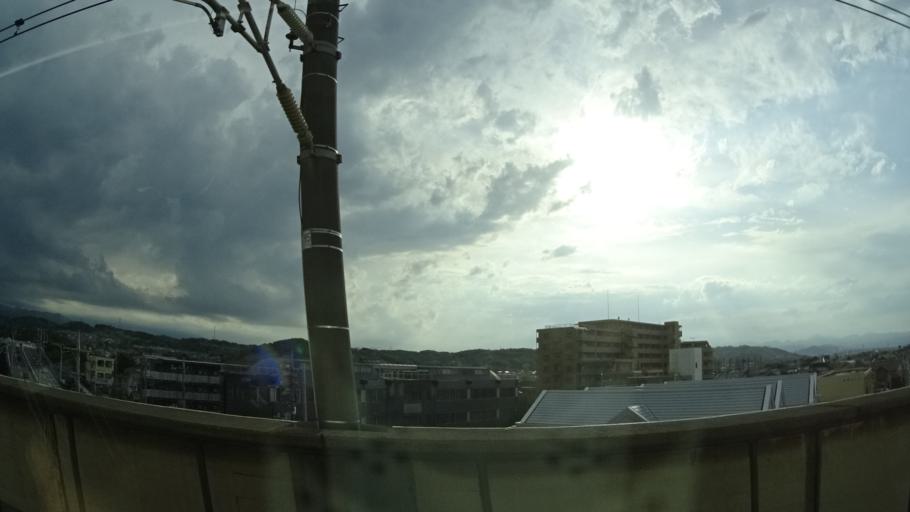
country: JP
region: Gunma
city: Takasaki
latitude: 36.3131
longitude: 139.0143
